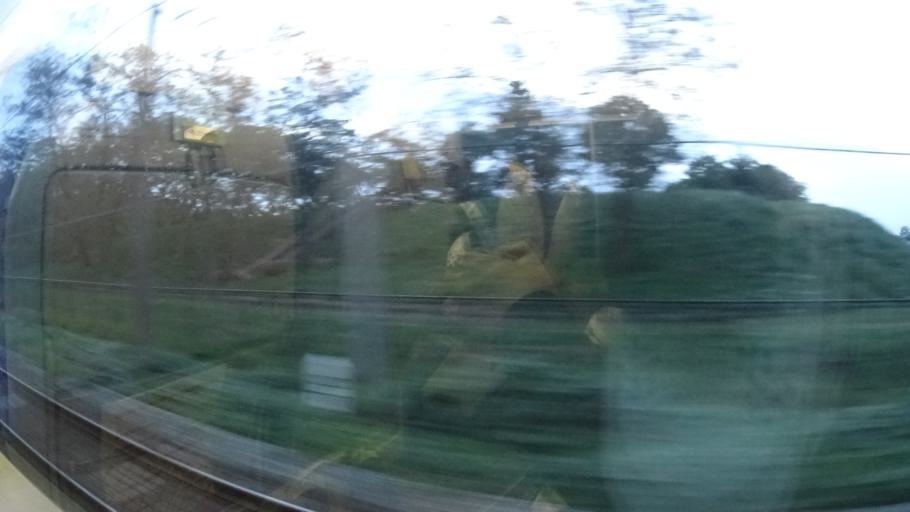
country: JP
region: Niigata
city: Shibata
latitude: 37.9513
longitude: 139.3420
